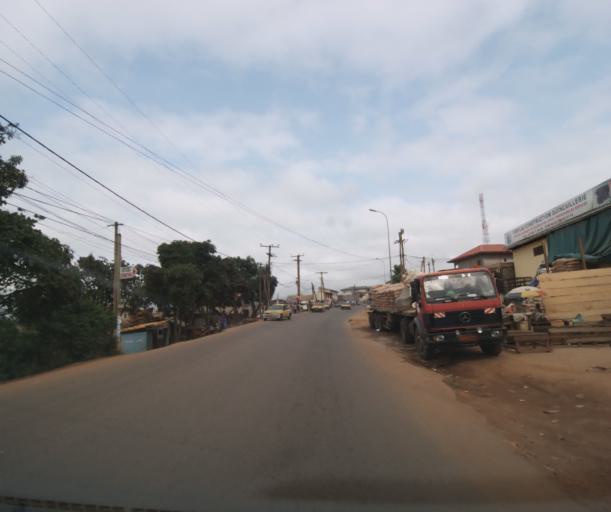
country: CM
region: Centre
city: Yaounde
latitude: 3.8010
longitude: 11.5280
